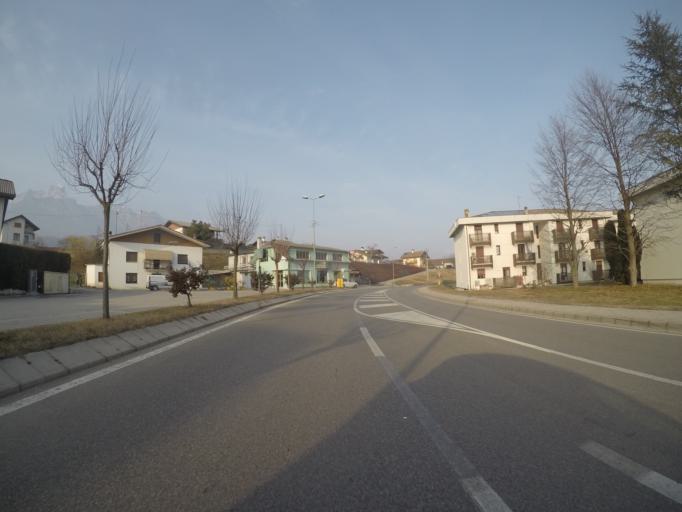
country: IT
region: Veneto
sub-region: Provincia di Belluno
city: Santa Giustina
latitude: 46.0864
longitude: 12.0455
